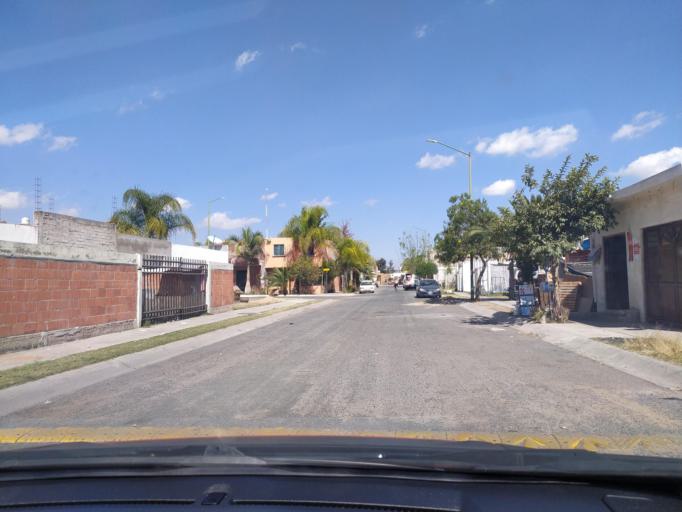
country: LA
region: Oudomxai
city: Muang La
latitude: 21.0295
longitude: 101.8279
